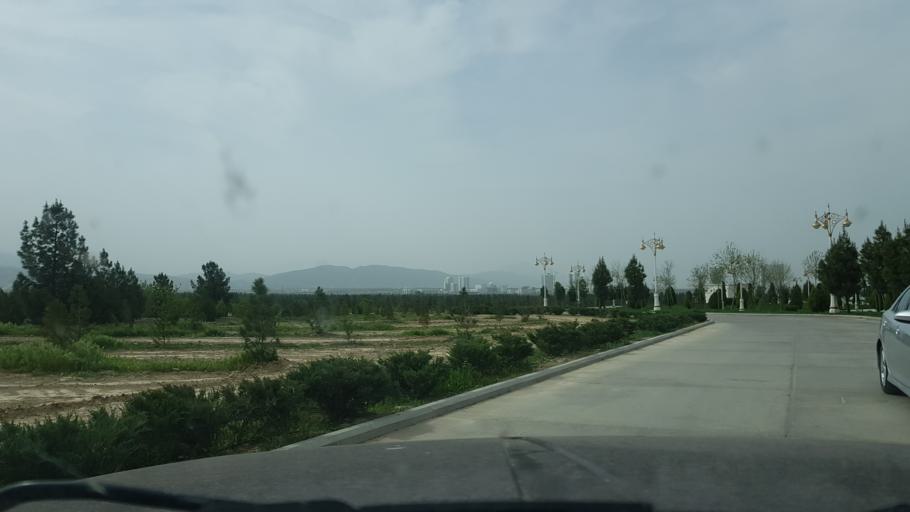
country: TM
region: Ahal
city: Ashgabat
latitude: 37.8812
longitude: 58.3312
